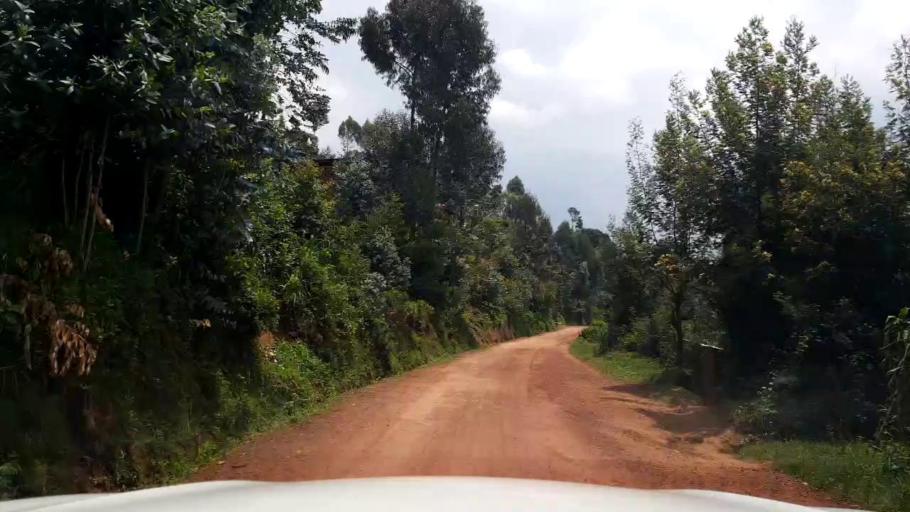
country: RW
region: Northern Province
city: Byumba
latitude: -1.4898
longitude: 29.9294
